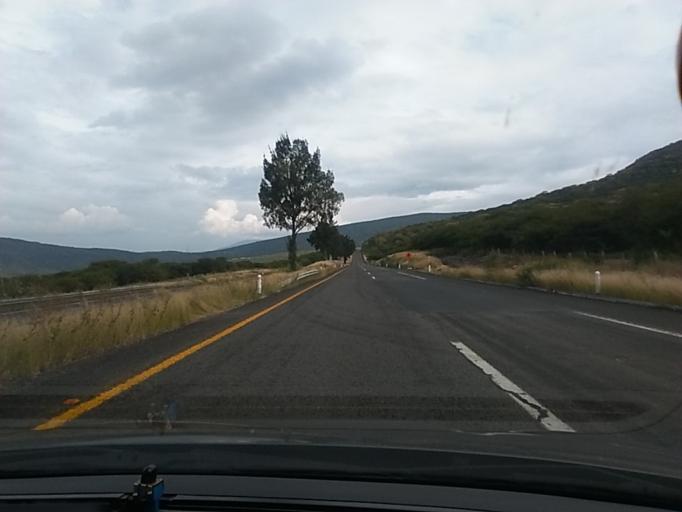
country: MX
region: Michoacan
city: Ixtlan
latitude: 20.2262
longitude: -102.3719
